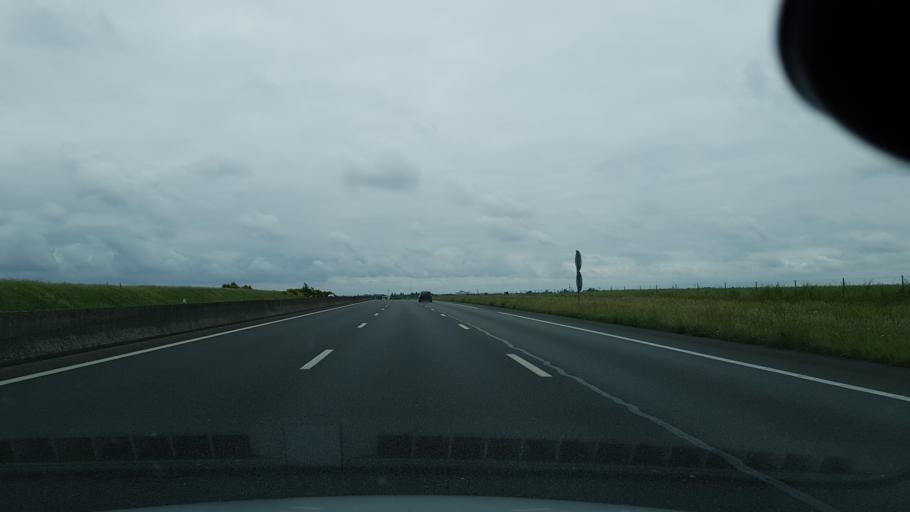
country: FR
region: Centre
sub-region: Departement du Loir-et-Cher
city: La Chaussee-Saint-Victor
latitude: 47.6401
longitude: 1.3612
